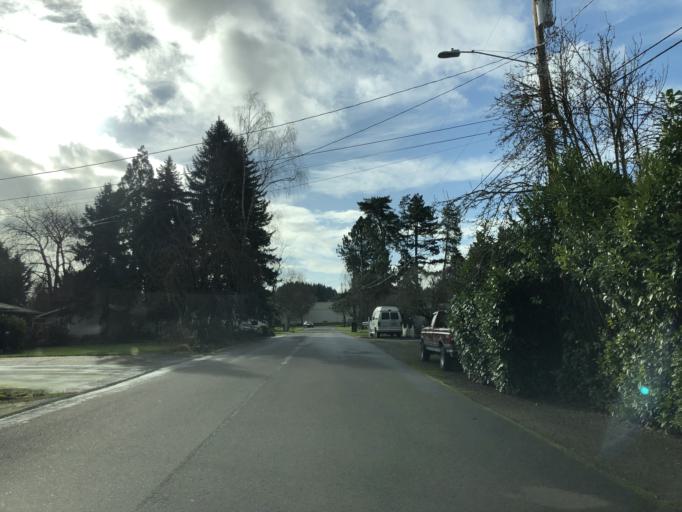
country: US
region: Oregon
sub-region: Washington County
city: Tigard
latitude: 45.4229
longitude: -122.7857
